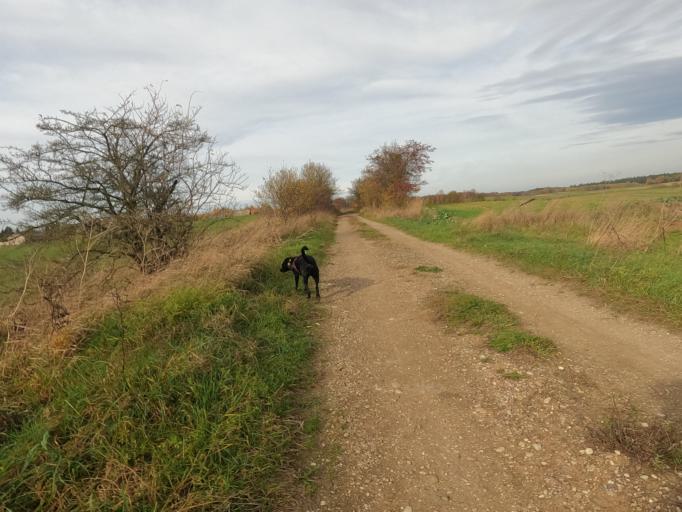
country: PL
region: Pomeranian Voivodeship
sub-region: Powiat starogardzki
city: Skarszewy
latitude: 54.0016
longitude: 18.4506
